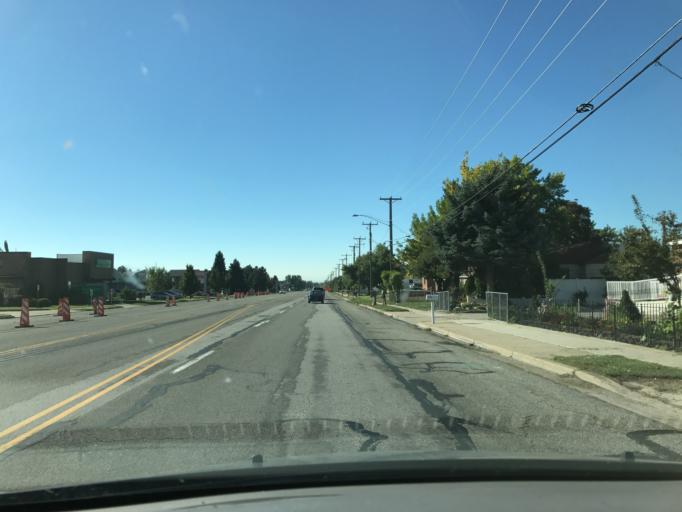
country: US
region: Utah
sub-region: Davis County
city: Hill Air Force Bace
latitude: 41.0870
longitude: -111.9735
